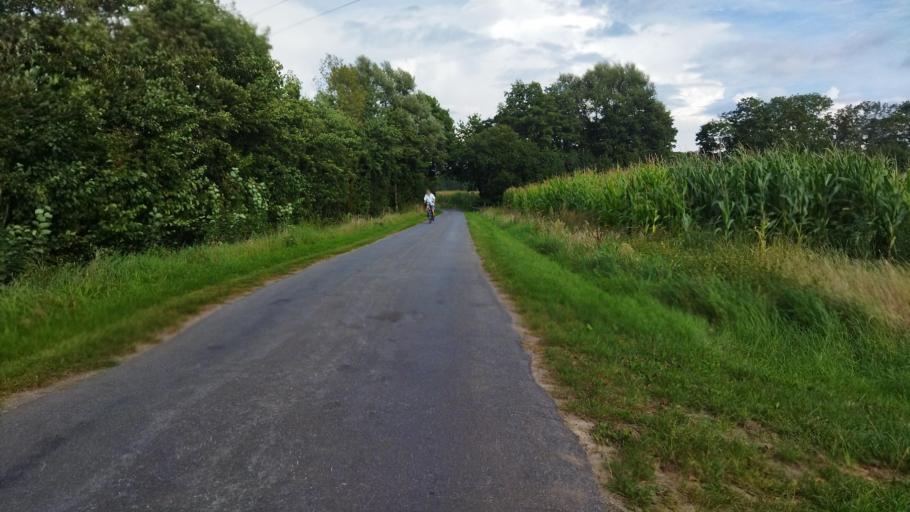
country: DE
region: North Rhine-Westphalia
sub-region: Regierungsbezirk Munster
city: Ostbevern
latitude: 52.0309
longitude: 7.8074
